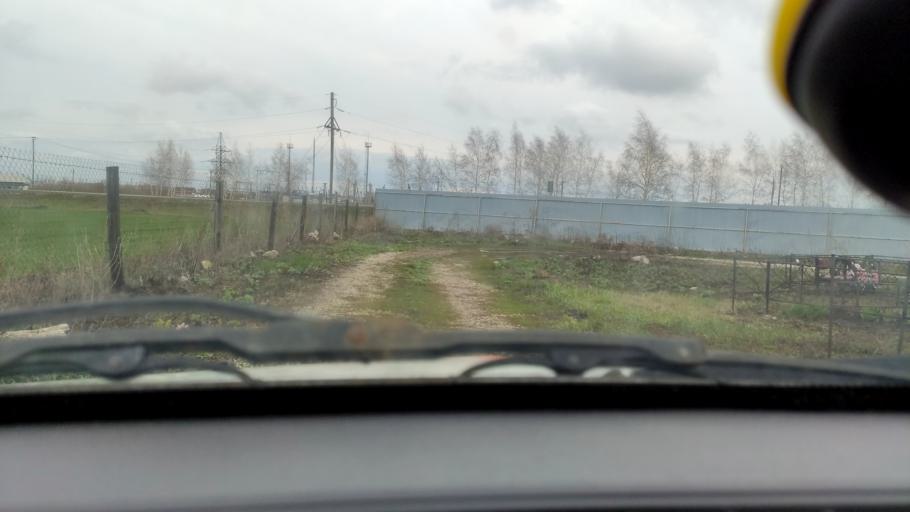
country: RU
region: Samara
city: Povolzhskiy
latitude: 53.6321
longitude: 49.6581
